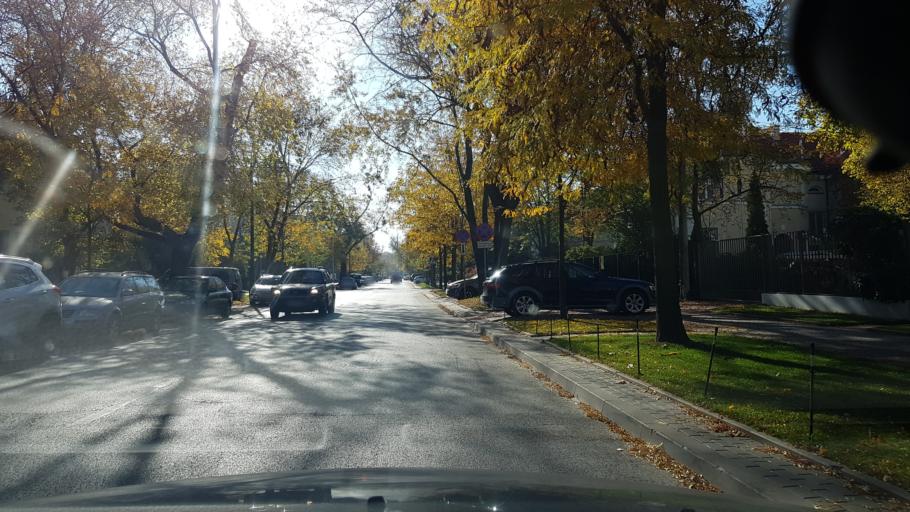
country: PL
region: Masovian Voivodeship
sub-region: Warszawa
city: Mokotow
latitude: 52.1933
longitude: 21.0204
